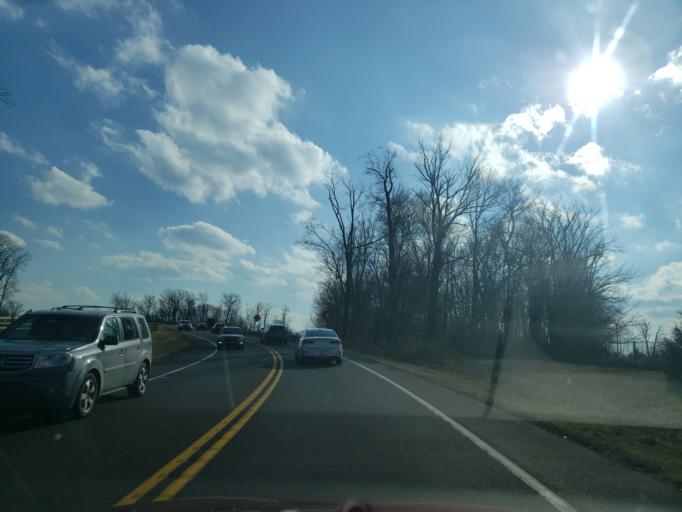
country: US
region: Pennsylvania
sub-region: Bucks County
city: Brittany Farms-Highlands
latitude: 40.2607
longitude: -75.2040
